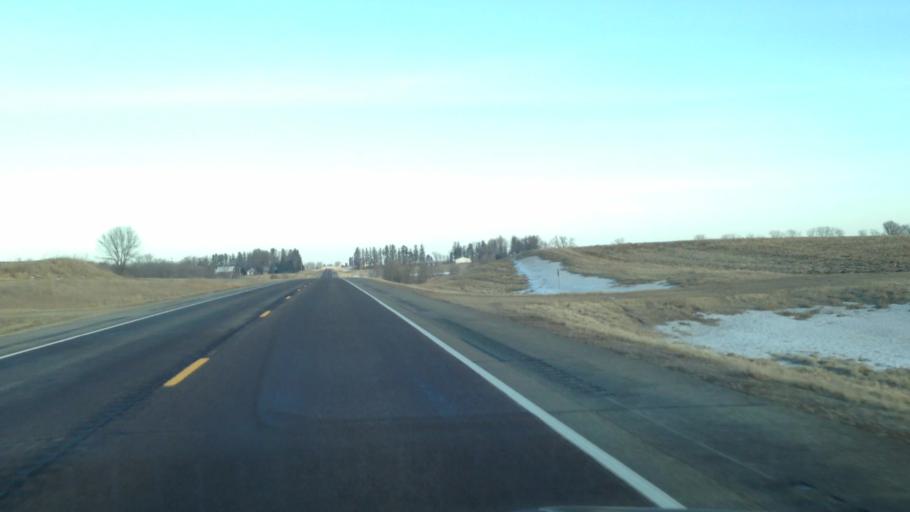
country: US
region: Minnesota
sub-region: Goodhue County
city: Goodhue
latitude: 44.3760
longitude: -92.6144
